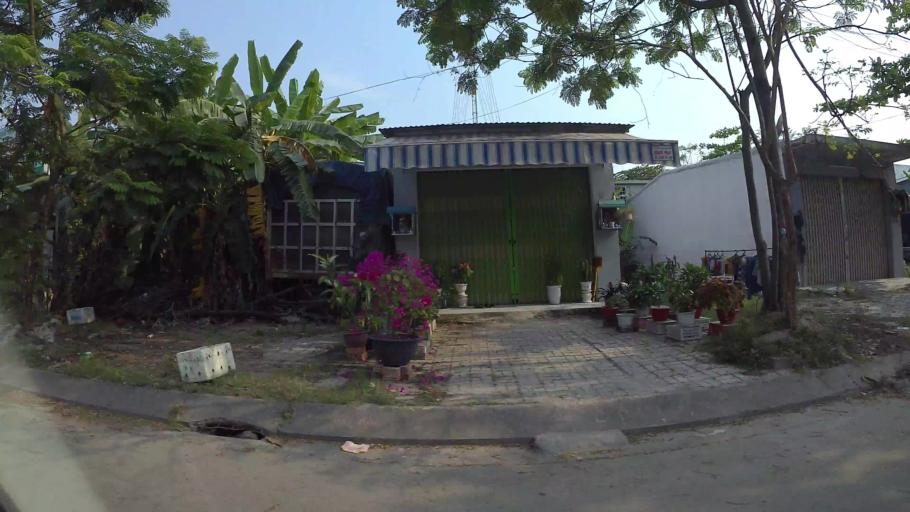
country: VN
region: Da Nang
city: Lien Chieu
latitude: 16.0533
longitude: 108.1662
